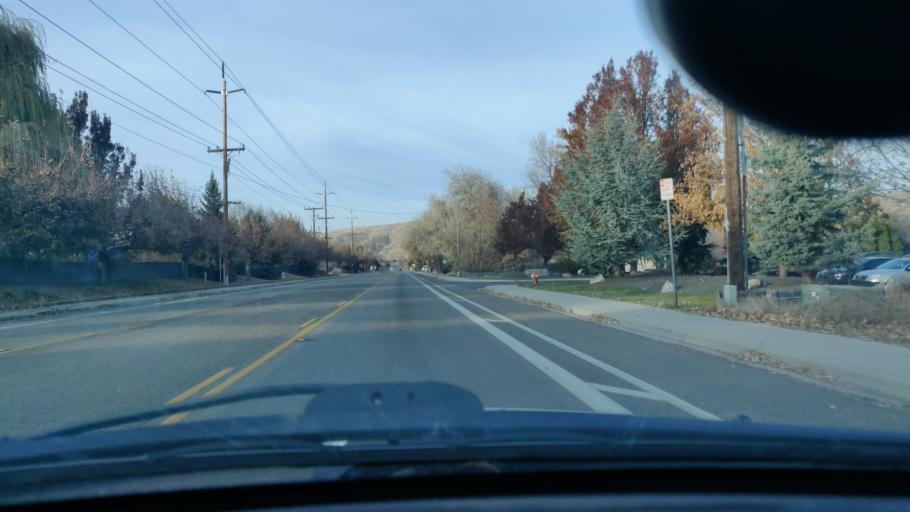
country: US
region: Idaho
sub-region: Ada County
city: Garden City
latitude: 43.6740
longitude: -116.2792
